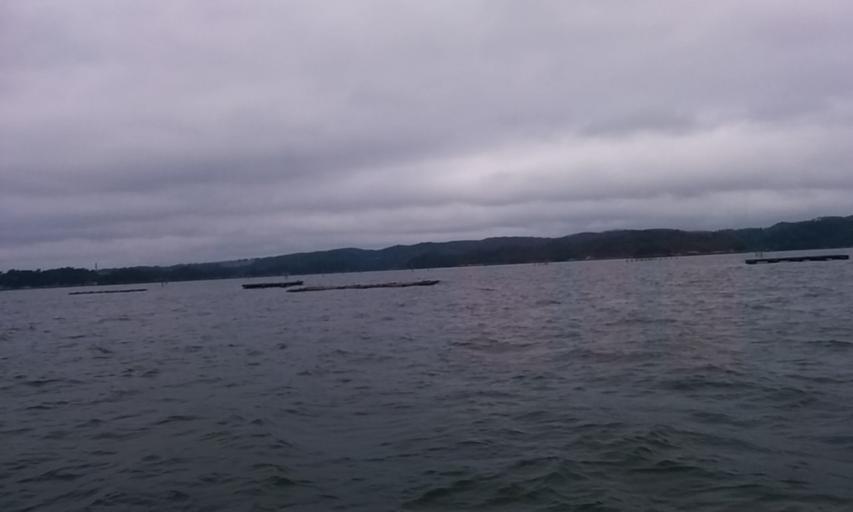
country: JP
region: Miyagi
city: Matsushima
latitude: 38.3406
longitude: 141.0734
